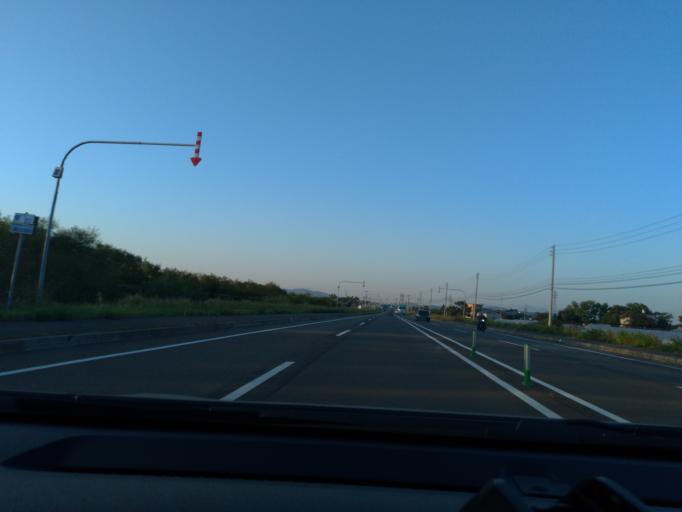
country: JP
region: Hokkaido
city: Tobetsu
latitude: 43.1866
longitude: 141.5240
